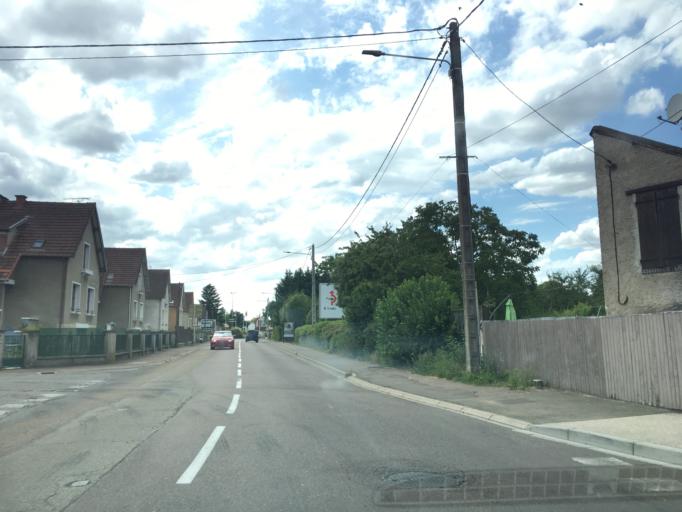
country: FR
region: Bourgogne
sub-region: Departement de l'Yonne
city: Joigny
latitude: 47.9783
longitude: 3.3889
